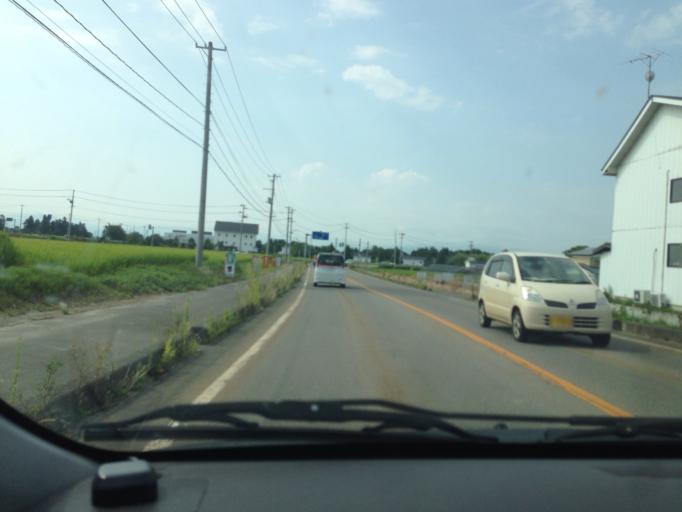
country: JP
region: Fukushima
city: Kitakata
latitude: 37.6396
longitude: 139.8559
